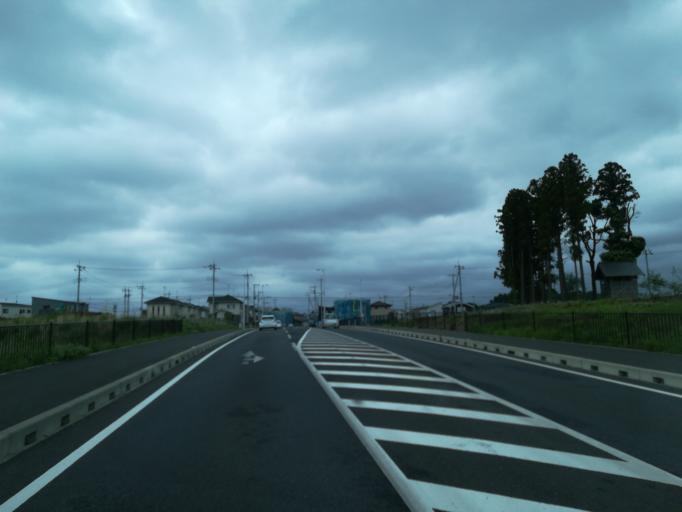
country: JP
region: Ibaraki
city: Naka
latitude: 36.1154
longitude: 140.1241
